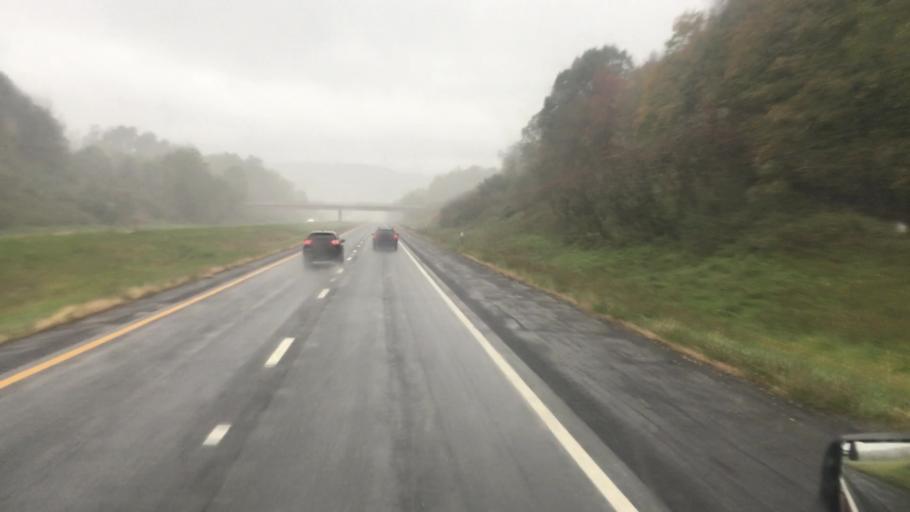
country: US
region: New York
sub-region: Chenango County
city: Bainbridge
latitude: 42.1847
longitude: -75.6016
